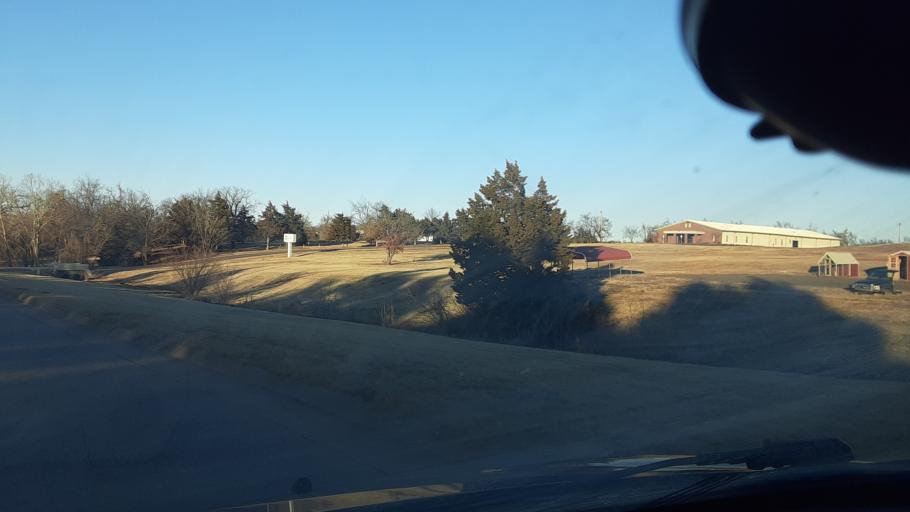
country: US
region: Oklahoma
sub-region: Logan County
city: Guthrie
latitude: 35.8331
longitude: -97.4254
